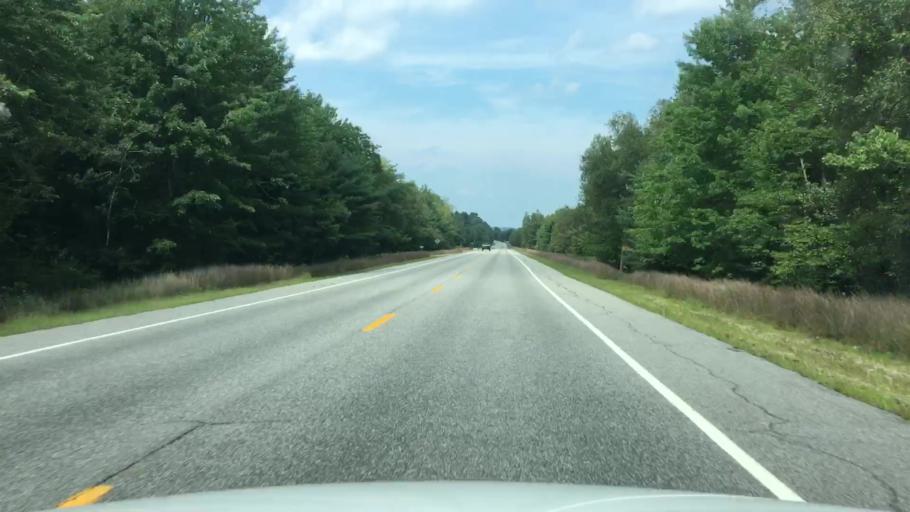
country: US
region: Maine
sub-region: Oxford County
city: Canton
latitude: 44.4243
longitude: -70.2960
